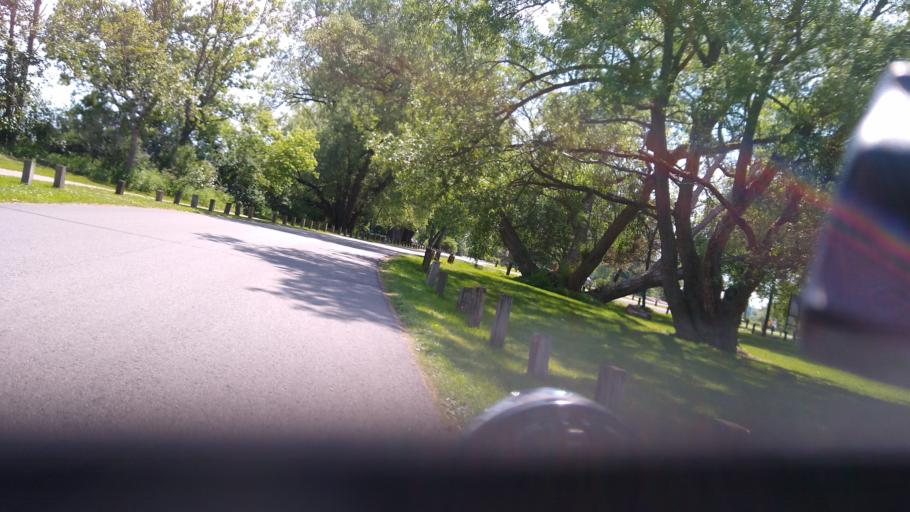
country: US
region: Michigan
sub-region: Delta County
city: Escanaba
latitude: 45.7413
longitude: -87.0433
